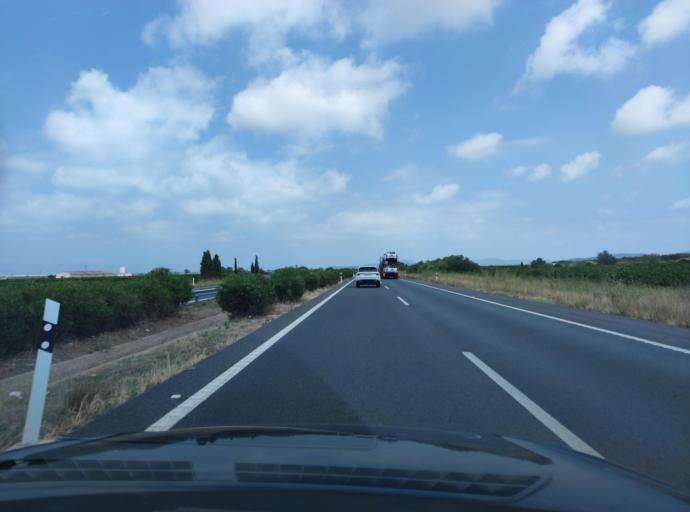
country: ES
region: Catalonia
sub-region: Provincia de Tarragona
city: Alcanar
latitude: 40.5131
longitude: 0.4154
